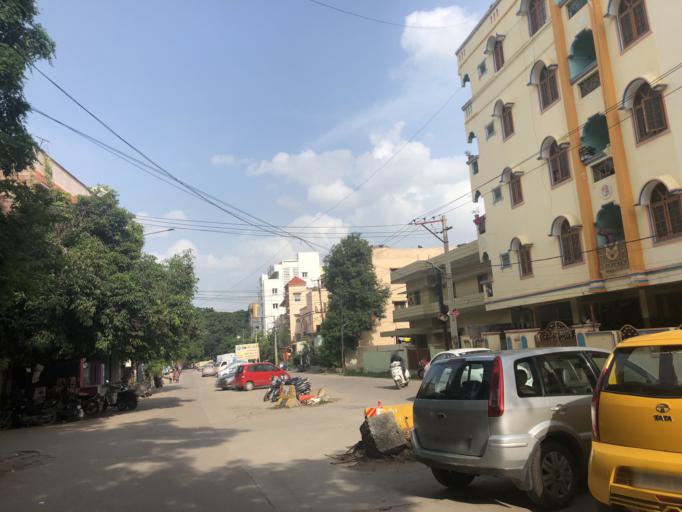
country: IN
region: Telangana
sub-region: Rangareddi
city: Kukatpalli
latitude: 17.4394
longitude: 78.4338
